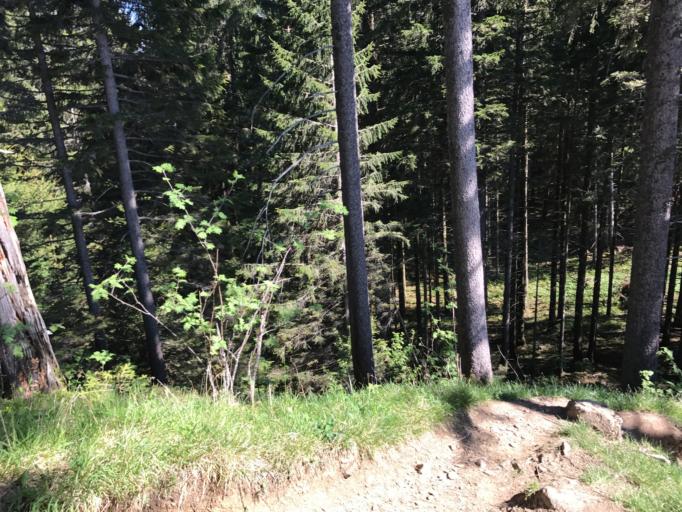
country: CH
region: Lucerne
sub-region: Lucerne-Land District
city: Kriens
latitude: 46.9935
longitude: 8.2548
